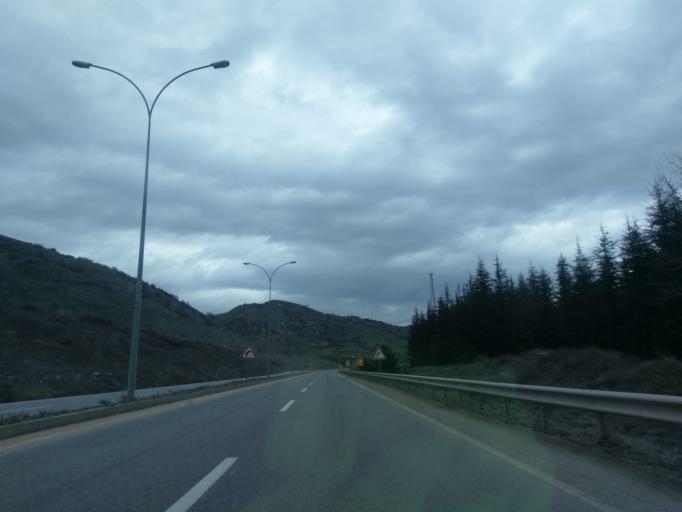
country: TR
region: Eskisehir
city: Eskisehir
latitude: 39.7427
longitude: 30.4276
